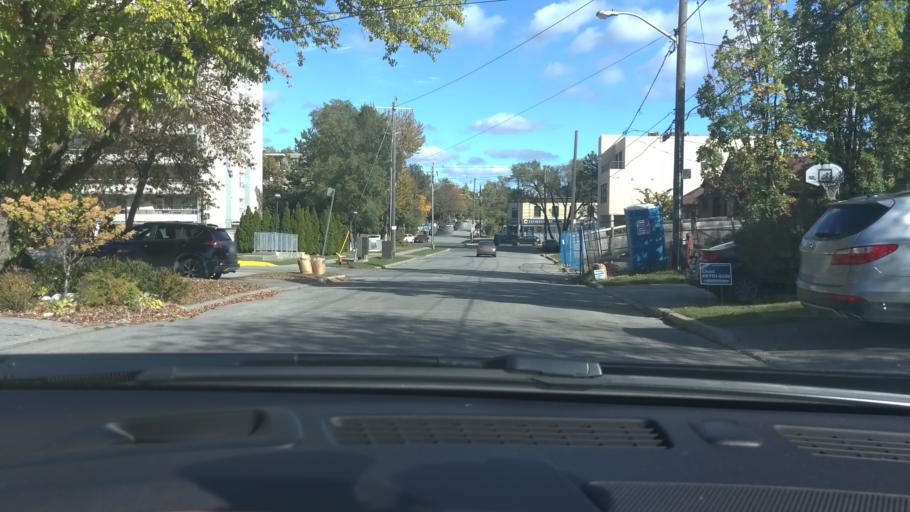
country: CA
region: Ontario
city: Toronto
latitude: 43.7139
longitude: -79.4299
